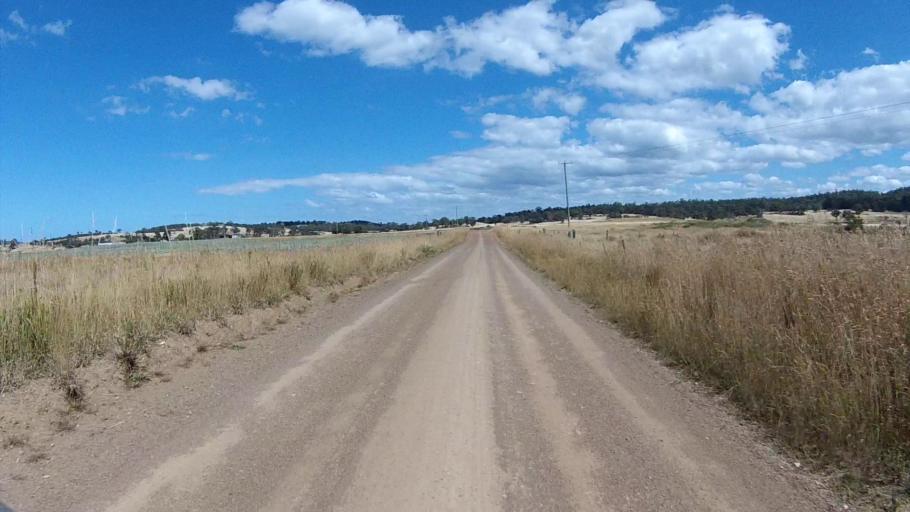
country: AU
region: Tasmania
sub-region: Break O'Day
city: St Helens
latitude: -41.9559
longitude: 148.0695
